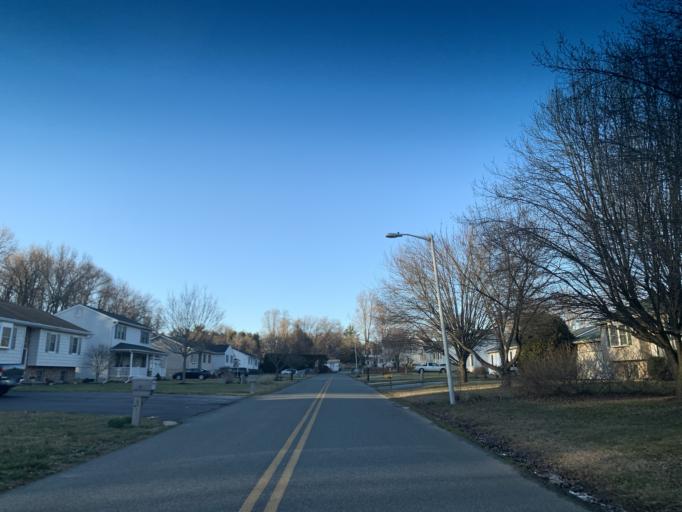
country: US
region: Maryland
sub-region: Cecil County
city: Perryville
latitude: 39.5651
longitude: -76.0735
